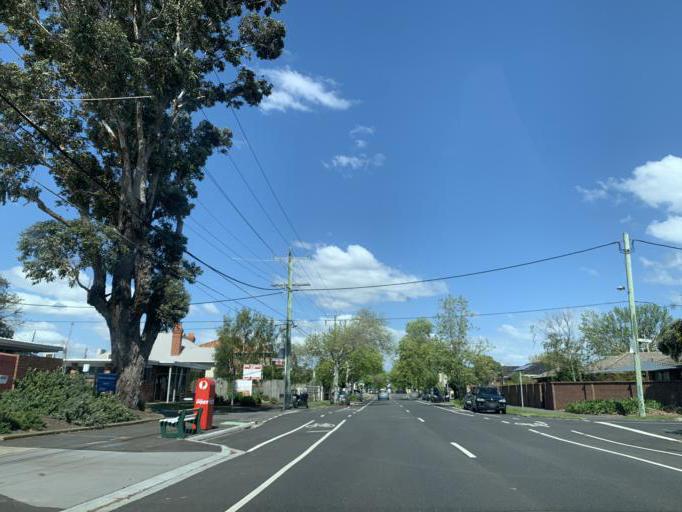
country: AU
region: Victoria
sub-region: Bayside
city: North Brighton
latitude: -37.9091
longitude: 145.0034
